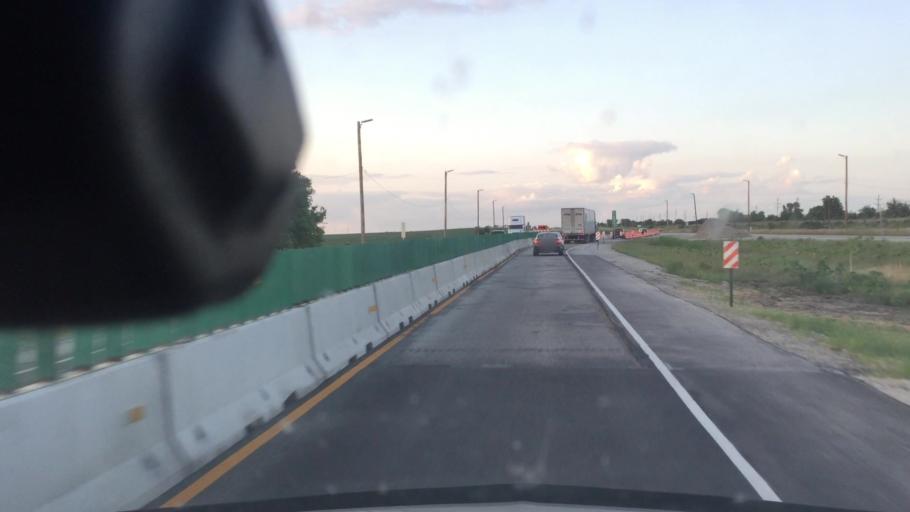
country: US
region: Illinois
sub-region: Livingston County
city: Odell
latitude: 40.9536
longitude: -88.5726
